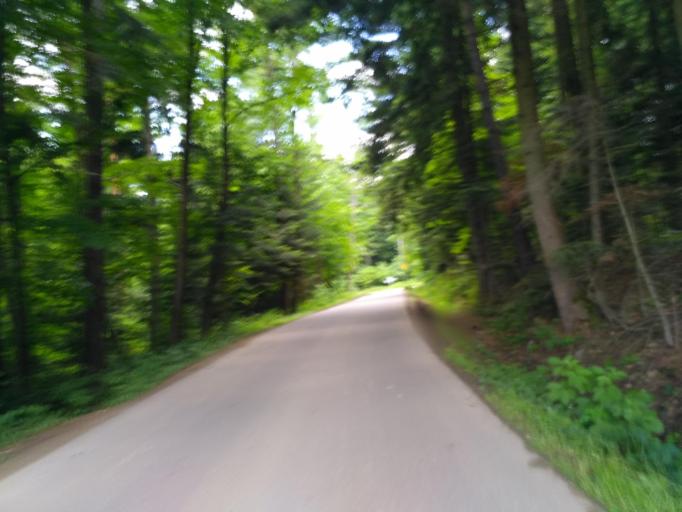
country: PL
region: Subcarpathian Voivodeship
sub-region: Powiat brzozowski
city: Wesola
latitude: 49.7597
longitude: 22.1291
